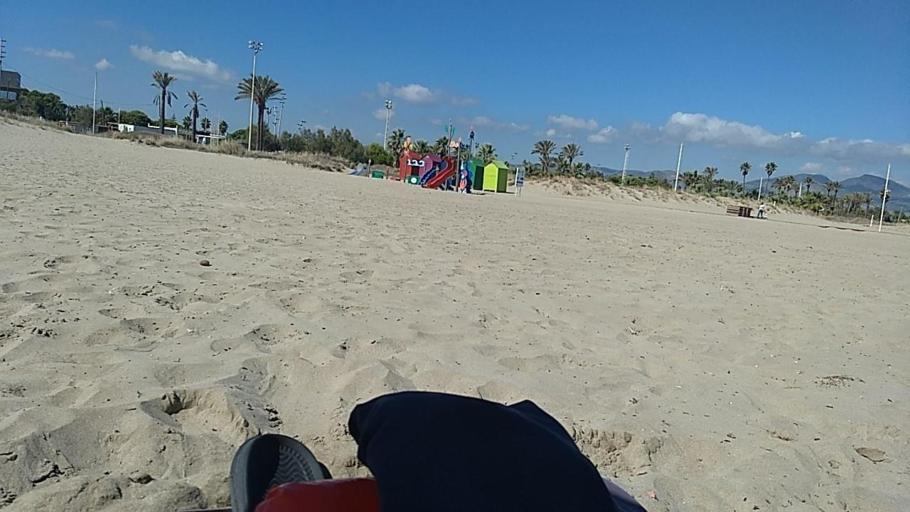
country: ES
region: Valencia
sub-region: Provincia de Castello
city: Castello de la Plana
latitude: 39.9797
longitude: 0.0243
